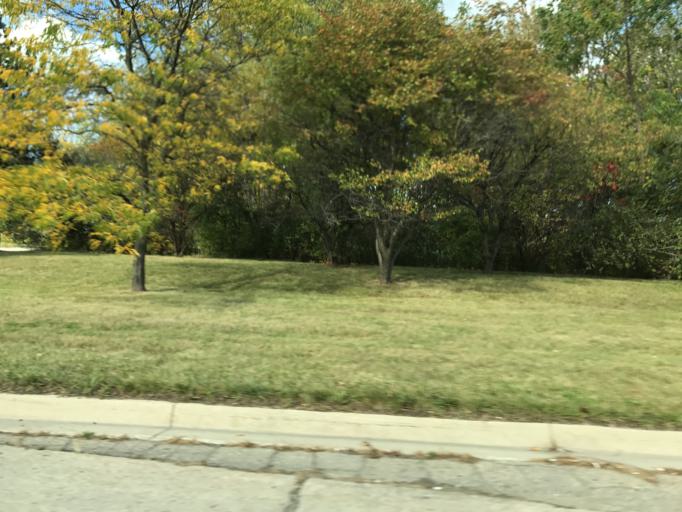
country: US
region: Michigan
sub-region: Oakland County
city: Wixom
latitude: 42.4972
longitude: -83.5489
